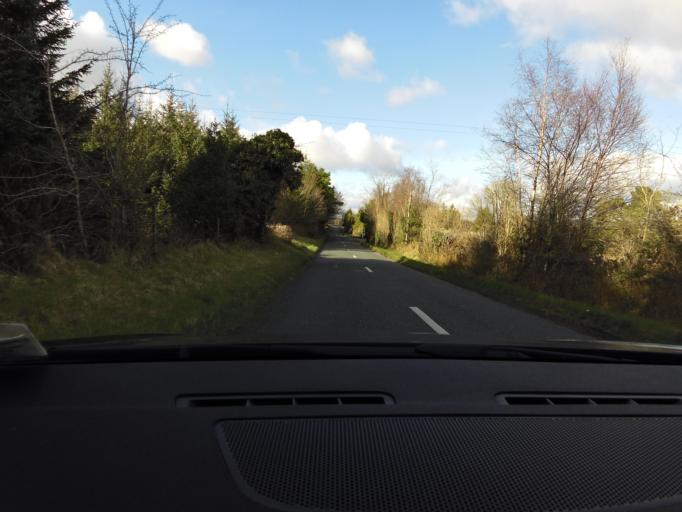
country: IE
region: Connaught
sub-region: County Galway
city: Athenry
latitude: 53.4548
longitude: -8.5502
